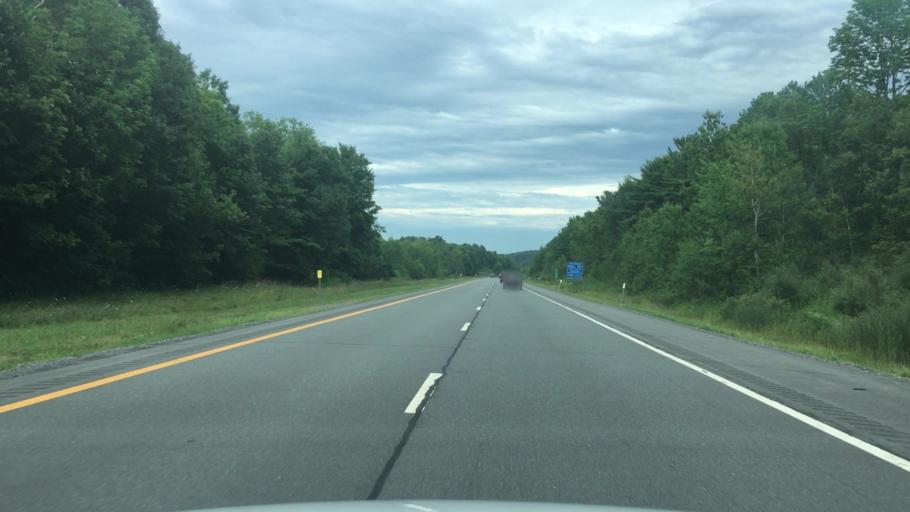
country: US
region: New York
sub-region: Schoharie County
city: Schoharie
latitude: 42.7249
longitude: -74.2168
